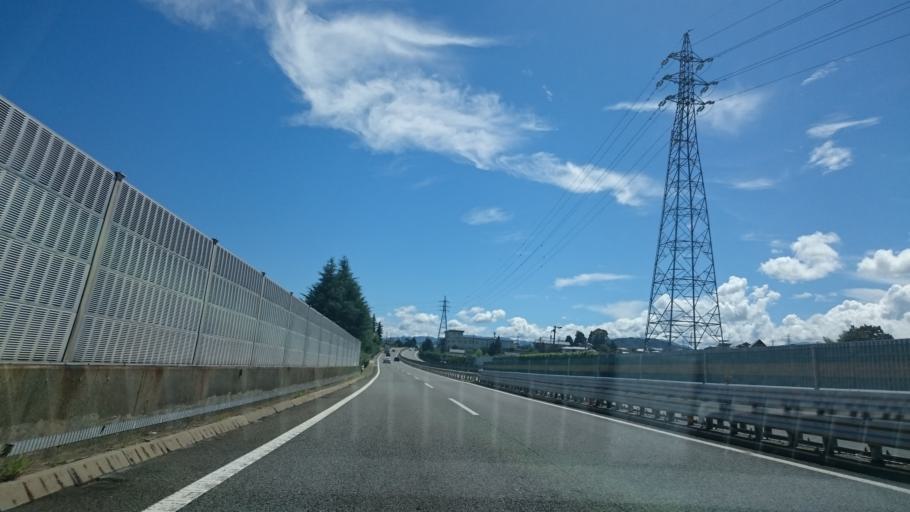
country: JP
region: Nagano
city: Iida
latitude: 35.5143
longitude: 137.8023
